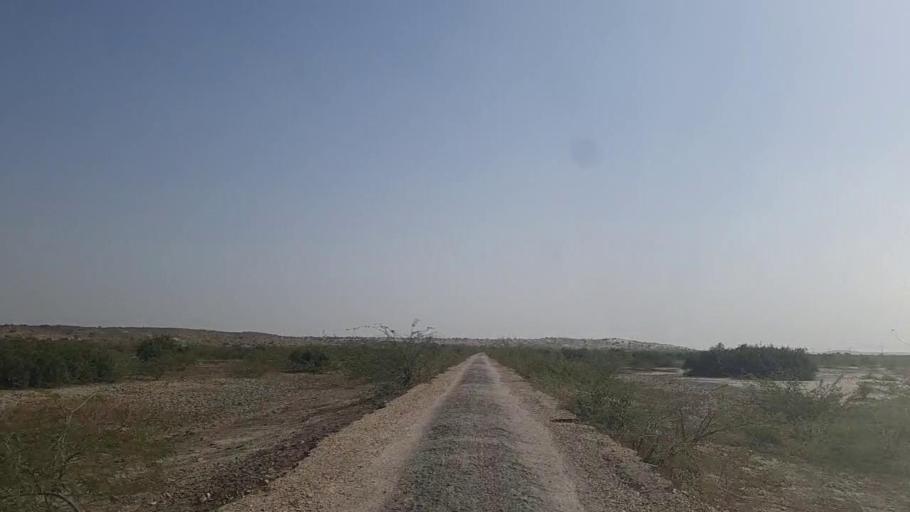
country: PK
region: Sindh
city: Naukot
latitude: 24.5834
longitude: 69.2931
